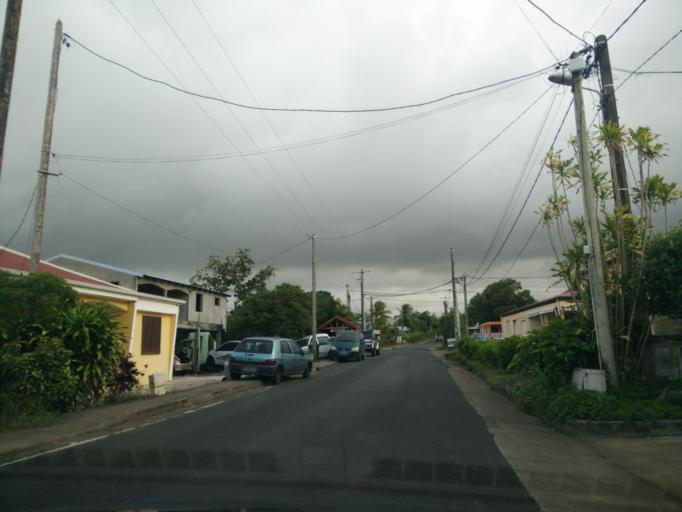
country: GP
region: Guadeloupe
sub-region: Guadeloupe
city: Petit-Bourg
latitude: 16.1861
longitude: -61.6157
